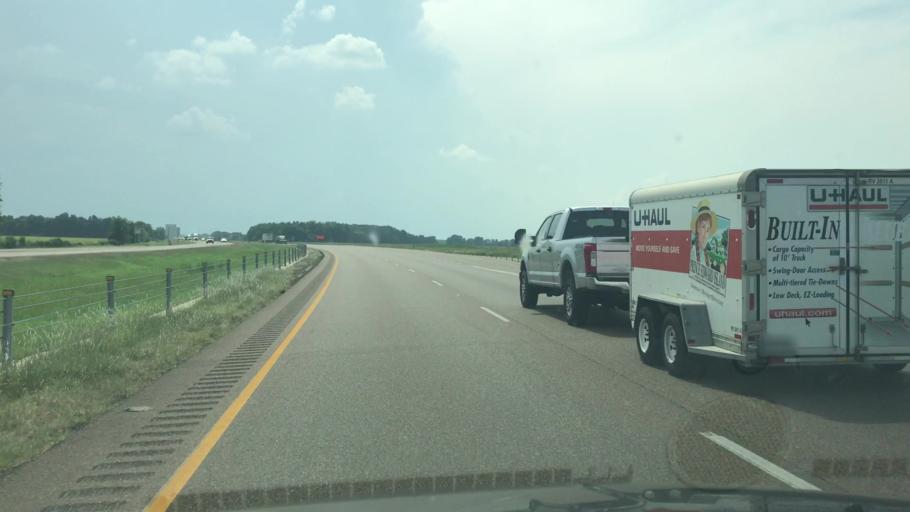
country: US
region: Arkansas
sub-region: Crittenden County
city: Earle
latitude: 35.1507
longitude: -90.4026
